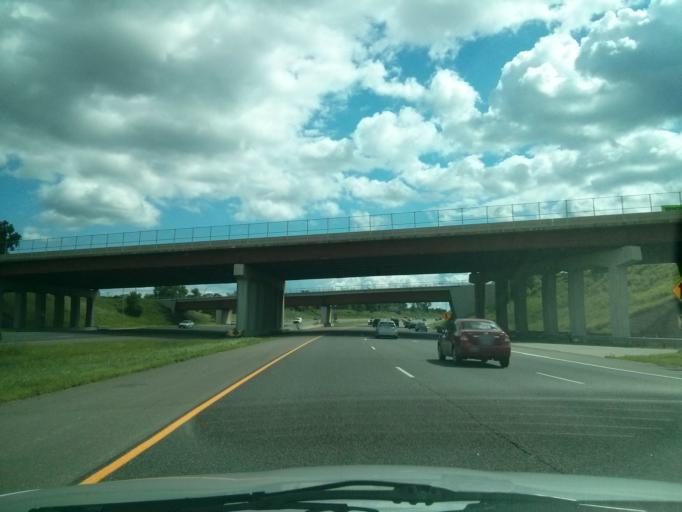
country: US
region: Minnesota
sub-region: Dakota County
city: Mendota Heights
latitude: 44.8596
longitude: -93.1459
